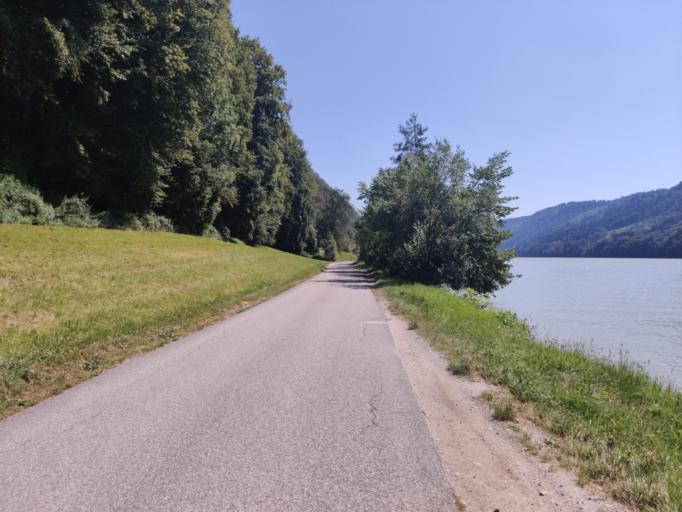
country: AT
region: Upper Austria
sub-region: Politischer Bezirk Rohrbach
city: Pfarrkirchen im Muehlkreis
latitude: 48.4571
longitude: 13.8190
